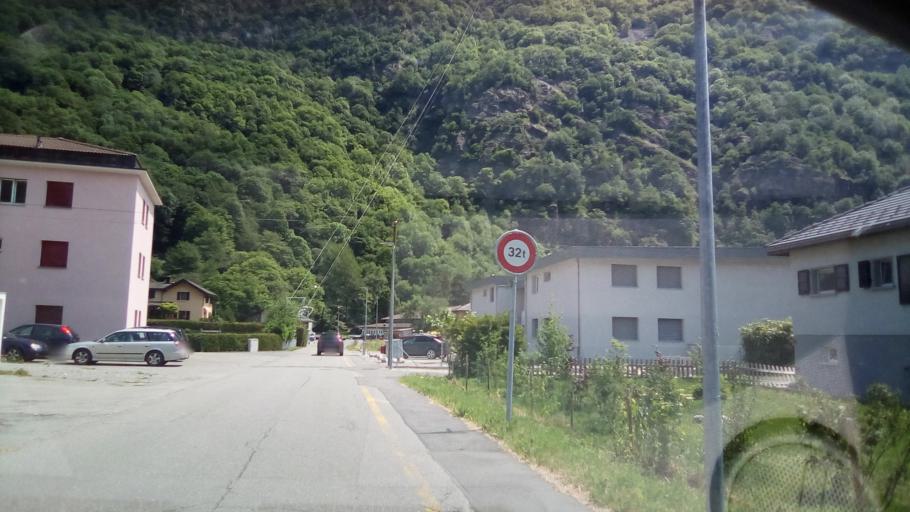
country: CH
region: Valais
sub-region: Saint-Maurice District
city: Vernayaz
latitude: 46.1502
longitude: 7.0426
